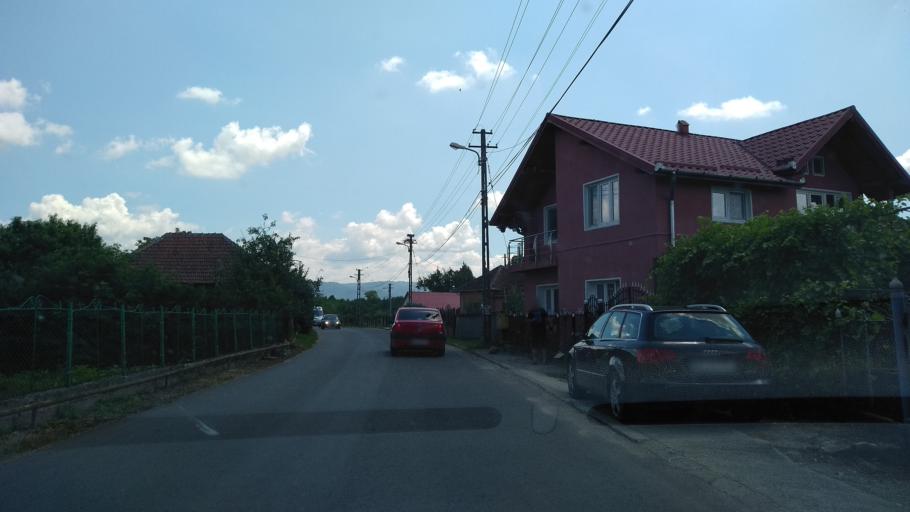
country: RO
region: Hunedoara
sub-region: Comuna Calan
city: Calan
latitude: 45.7195
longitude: 23.0337
